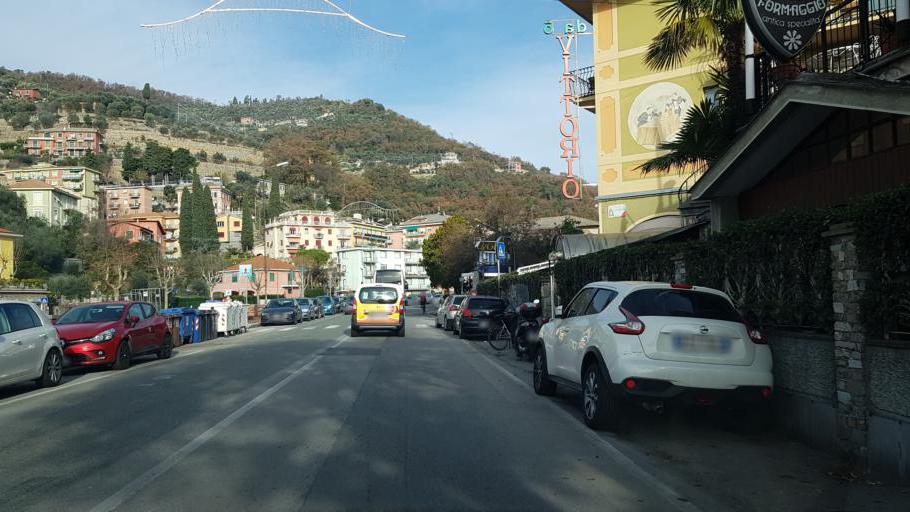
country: IT
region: Liguria
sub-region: Provincia di Genova
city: Recco
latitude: 44.3663
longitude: 9.1466
